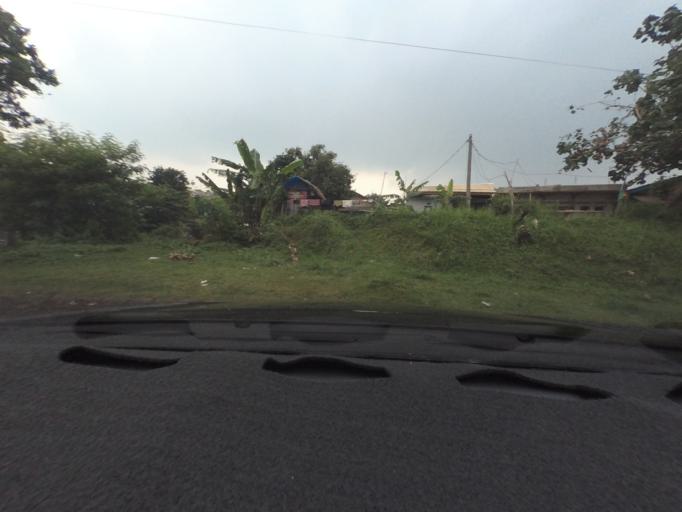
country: ID
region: West Java
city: Bogor
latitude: -6.5990
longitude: 106.8214
